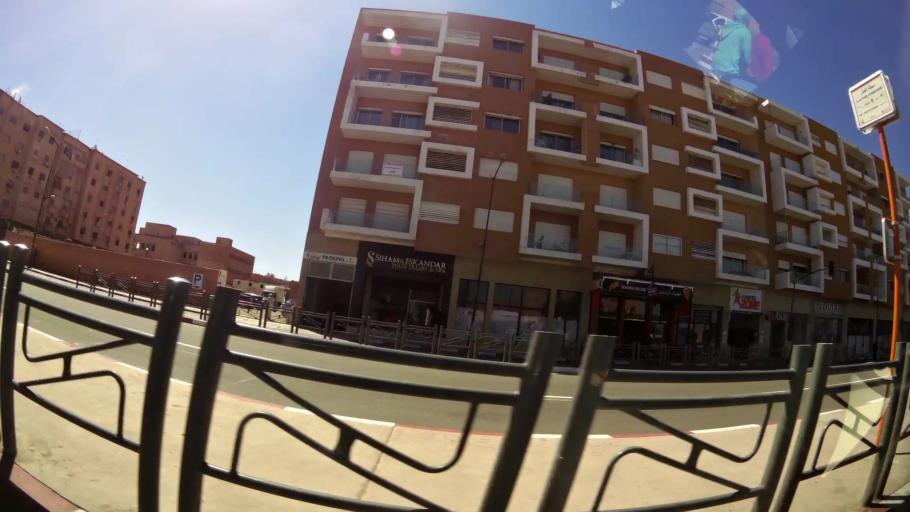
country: MA
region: Marrakech-Tensift-Al Haouz
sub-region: Marrakech
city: Marrakesh
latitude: 31.6298
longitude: -8.0187
